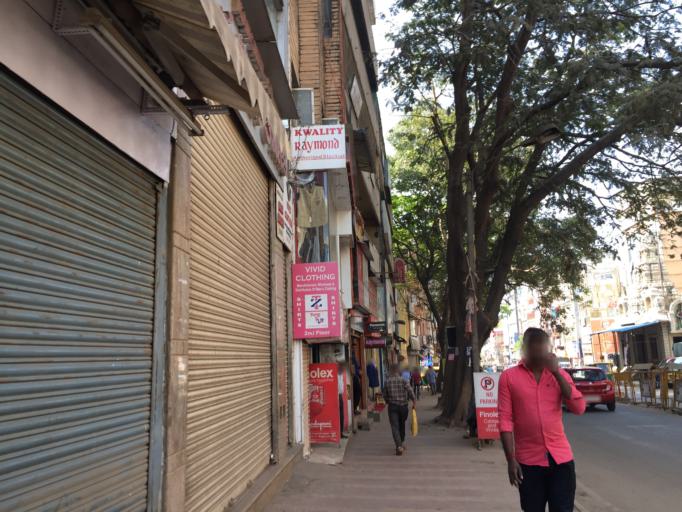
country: IN
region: Karnataka
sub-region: Bangalore Urban
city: Bangalore
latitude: 12.9713
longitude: 77.5765
